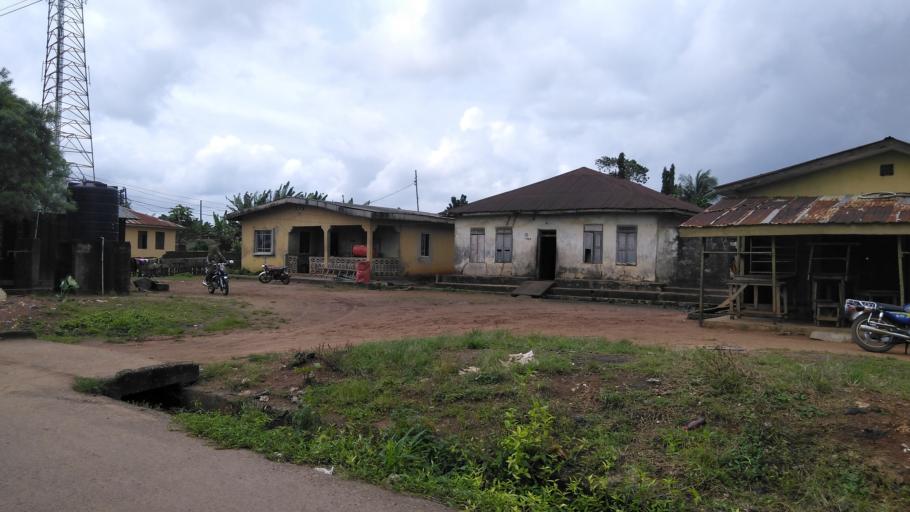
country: NG
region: Ogun
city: Abigi
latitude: 6.6016
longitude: 4.4906
